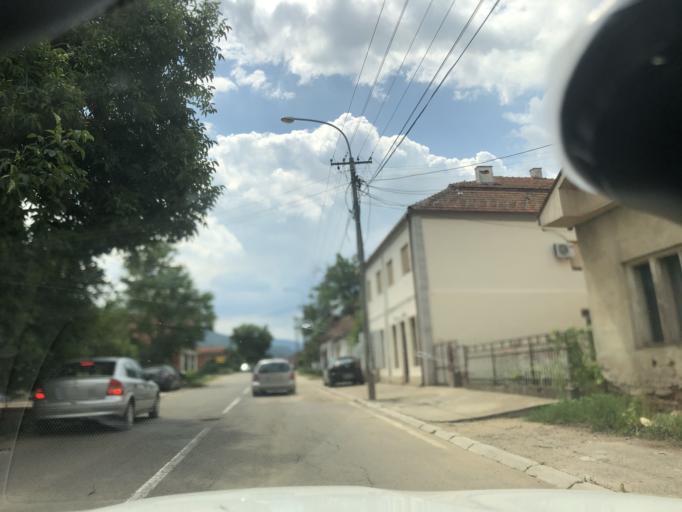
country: RS
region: Central Serbia
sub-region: Jablanicki Okrug
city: Medvega
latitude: 42.8378
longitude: 21.5846
